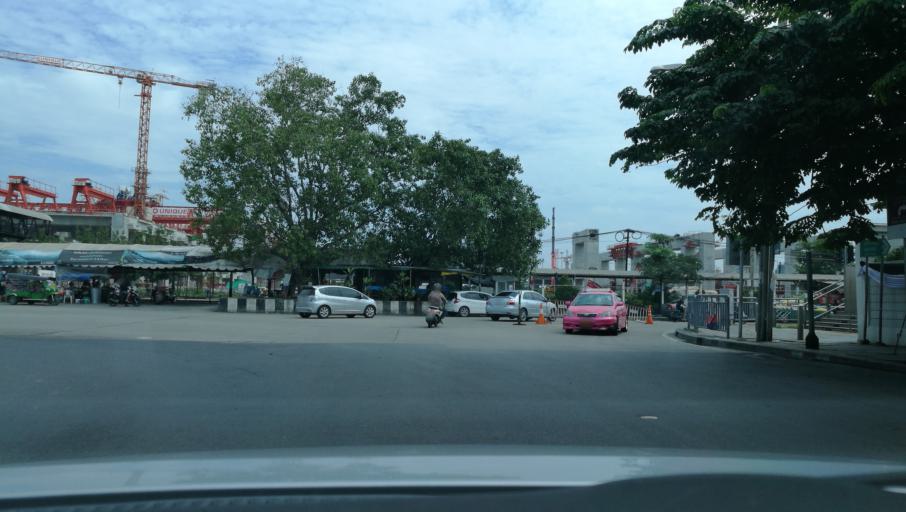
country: TH
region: Bangkok
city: Bang Sue
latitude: 13.8031
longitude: 100.5390
